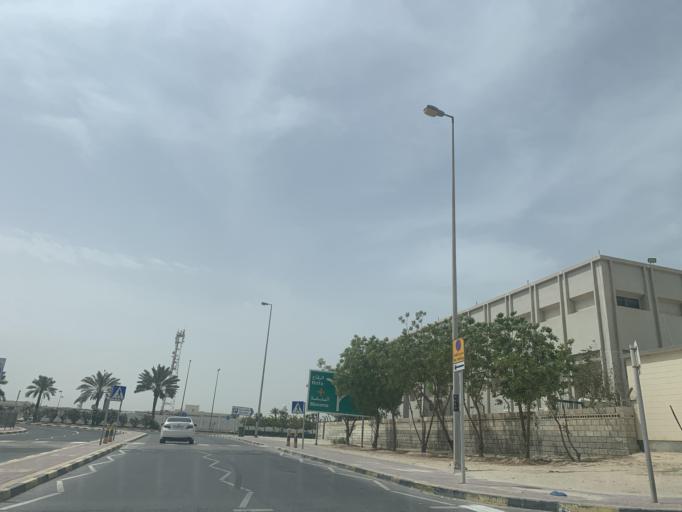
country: BH
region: Northern
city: Madinat `Isa
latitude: 26.1584
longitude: 50.5399
